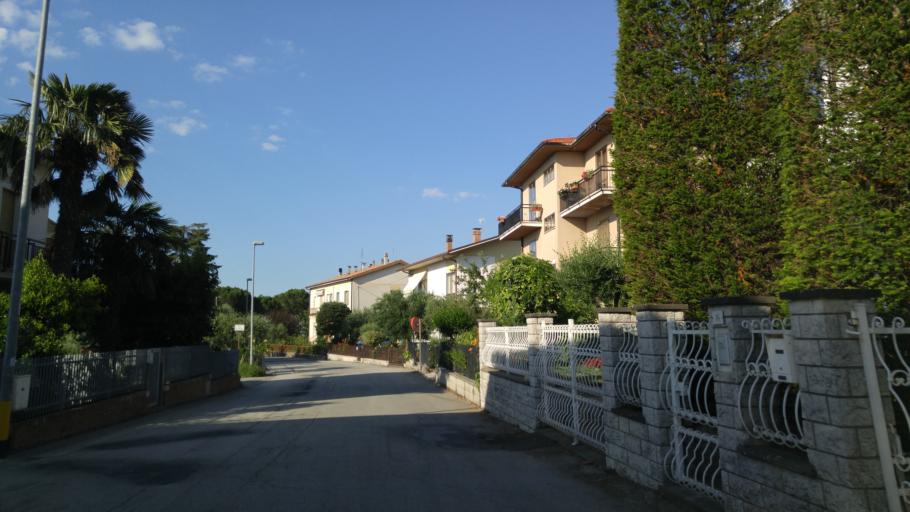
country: IT
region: The Marches
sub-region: Provincia di Pesaro e Urbino
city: Sant'Ippolito
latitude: 43.6891
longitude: 12.8724
